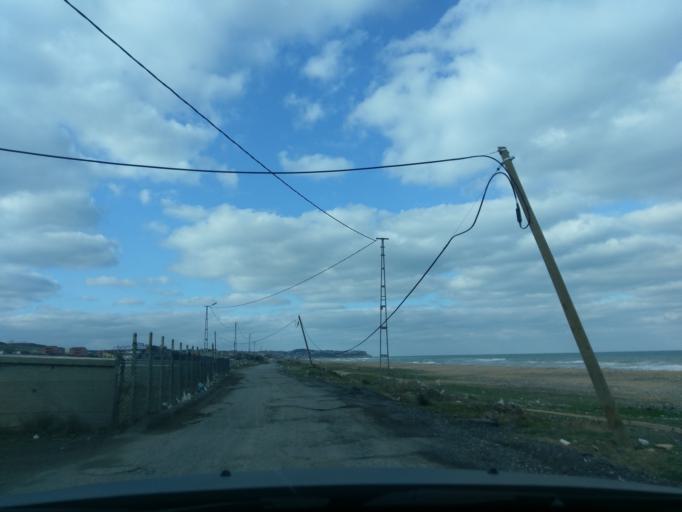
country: TR
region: Istanbul
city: Durusu
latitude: 41.3244
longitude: 28.7286
